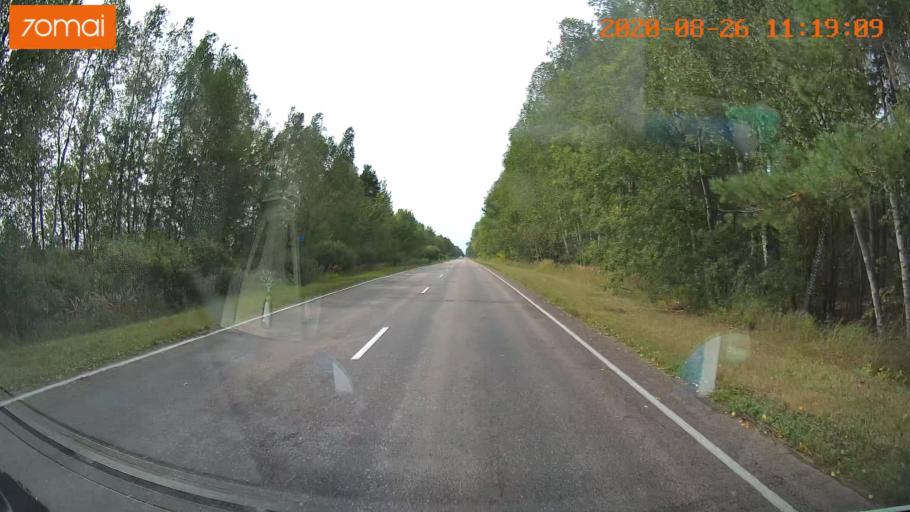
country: RU
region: Rjazan
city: Shilovo
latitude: 54.4024
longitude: 41.0848
